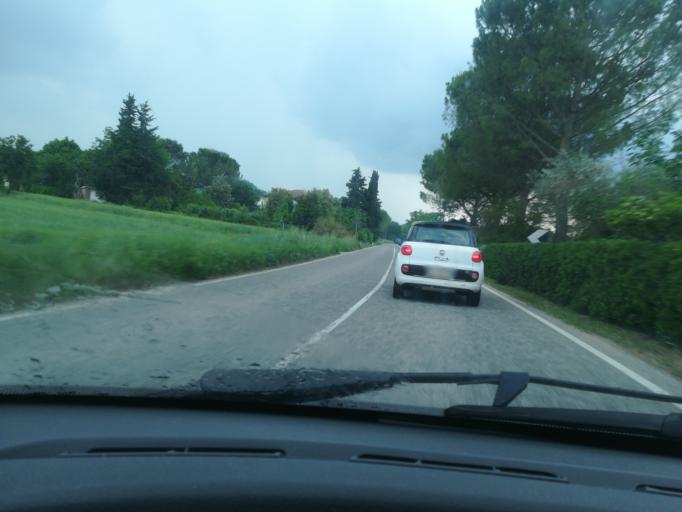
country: IT
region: The Marches
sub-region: Provincia di Macerata
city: Pollenza
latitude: 43.2919
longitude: 13.3638
